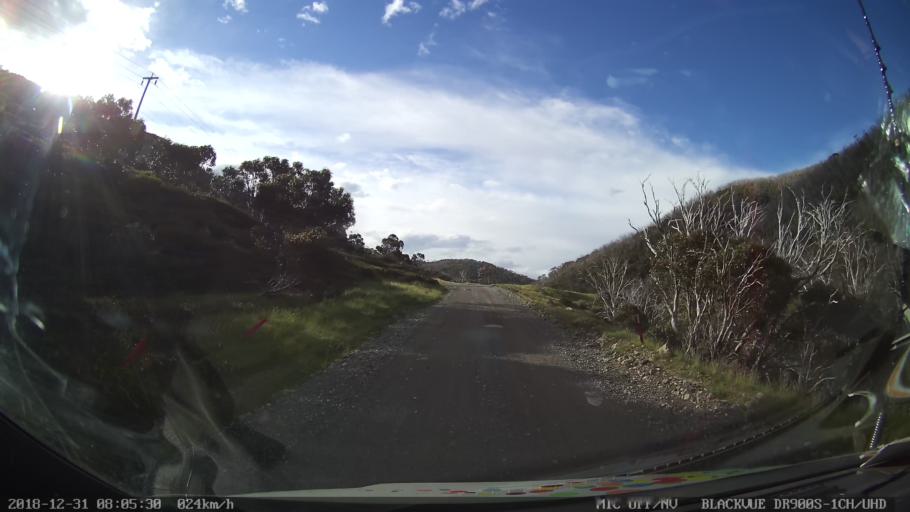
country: AU
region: New South Wales
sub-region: Snowy River
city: Jindabyne
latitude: -36.3713
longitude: 148.4066
